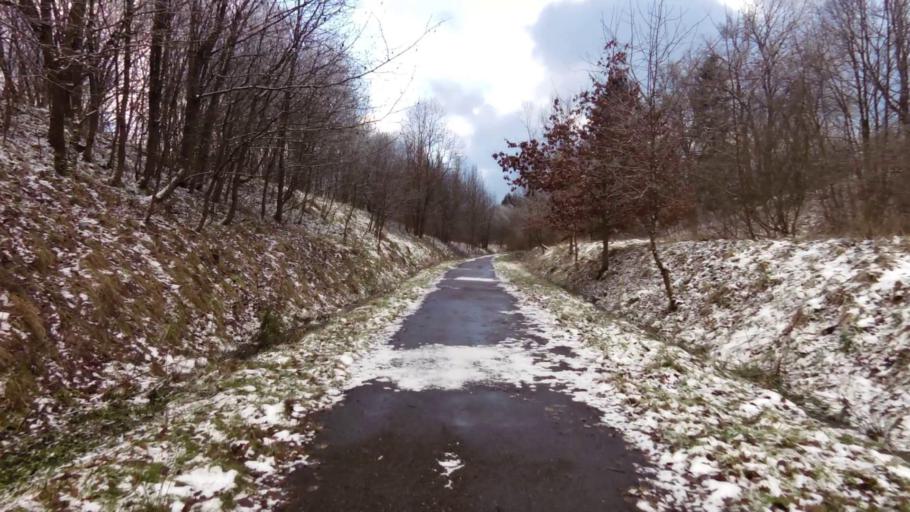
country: PL
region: West Pomeranian Voivodeship
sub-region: Powiat swidwinski
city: Polczyn-Zdroj
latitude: 53.7297
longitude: 16.0437
